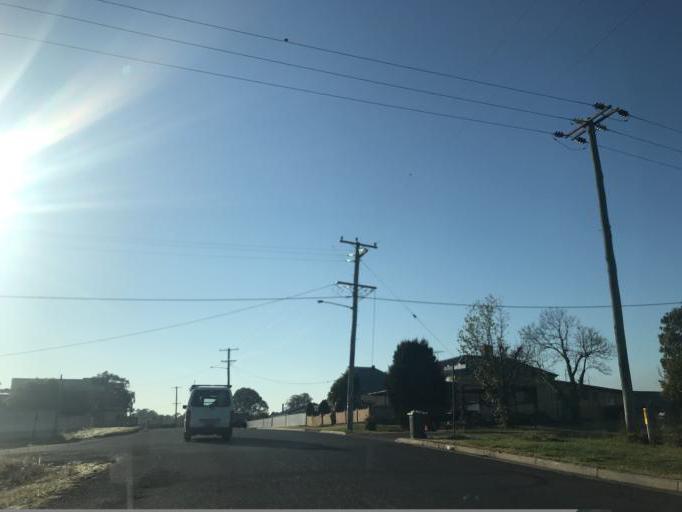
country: AU
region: New South Wales
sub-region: Cessnock
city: Cessnock
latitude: -32.9142
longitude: 151.3050
